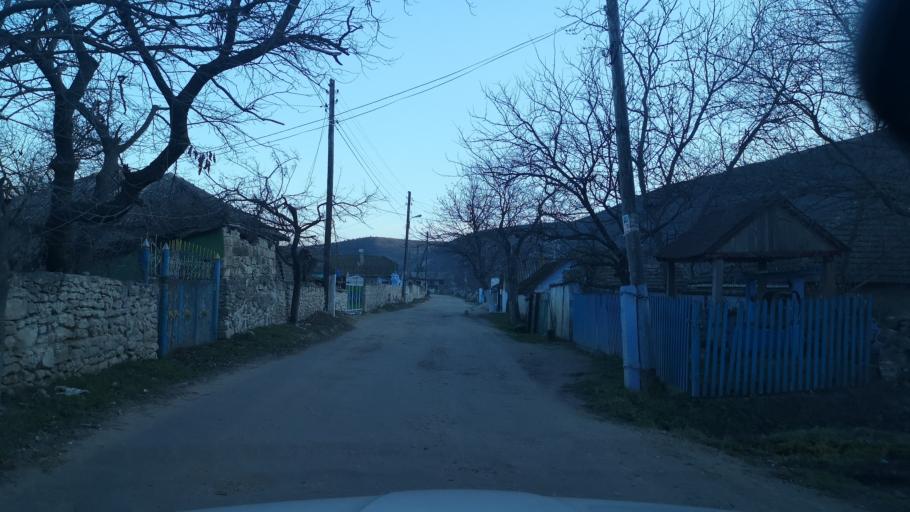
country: MD
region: Telenesti
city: Cocieri
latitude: 47.3041
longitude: 28.9627
